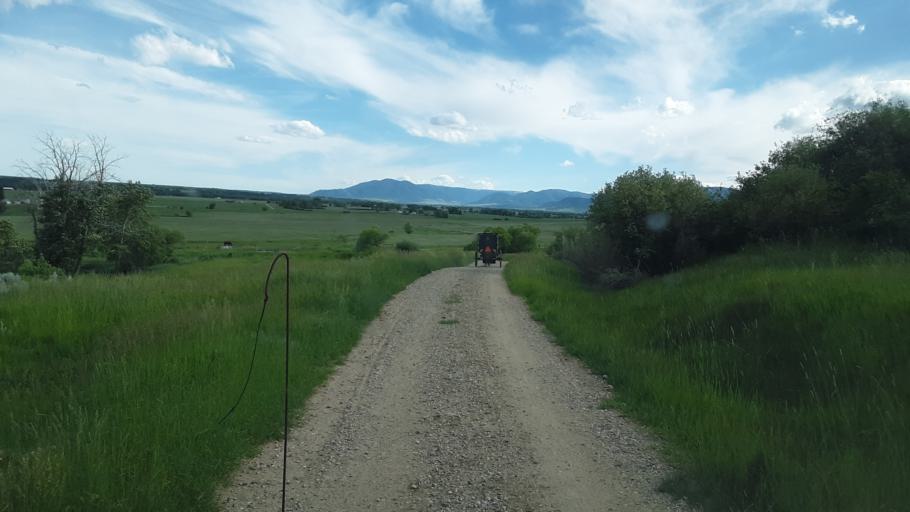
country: US
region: Montana
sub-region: Carbon County
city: Red Lodge
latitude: 45.3652
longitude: -109.1912
